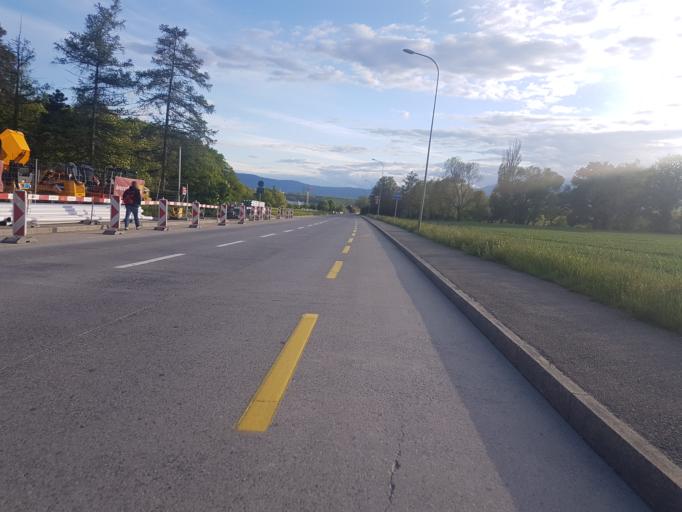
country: CH
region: Geneva
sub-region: Geneva
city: Vernier
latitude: 46.2074
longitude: 6.0679
